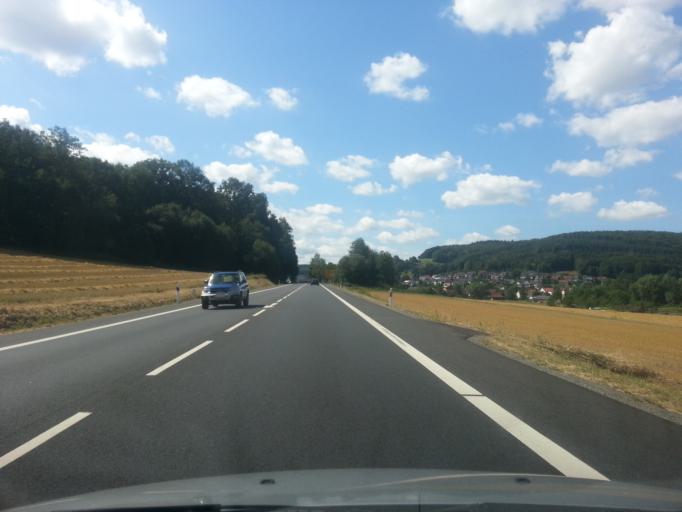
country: DE
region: Hesse
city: Hochst im Odenwald
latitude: 49.7757
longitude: 8.9926
